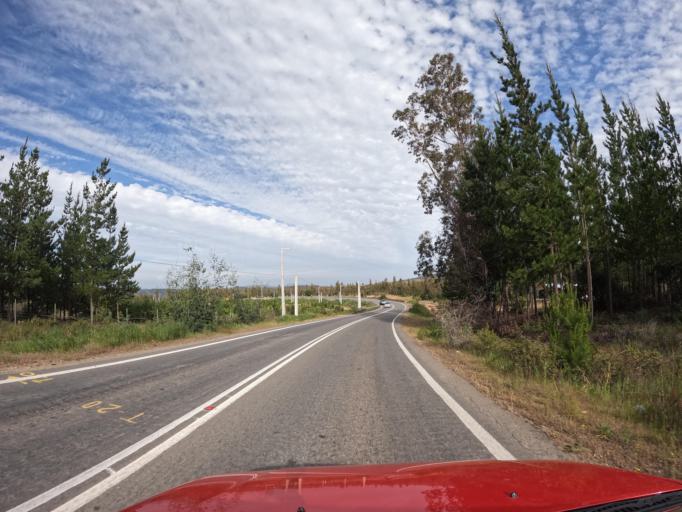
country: CL
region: O'Higgins
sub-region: Provincia de Colchagua
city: Santa Cruz
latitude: -34.2966
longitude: -71.8151
